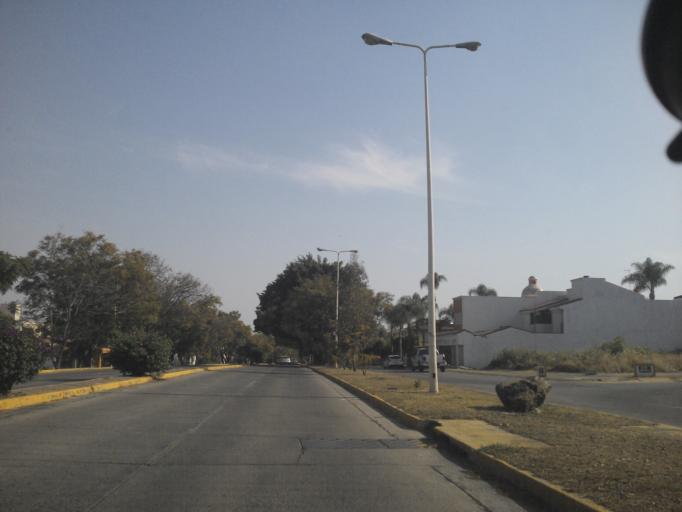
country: MX
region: Jalisco
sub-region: Tlajomulco de Zuniga
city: Palomar
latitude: 20.6047
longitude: -103.4483
